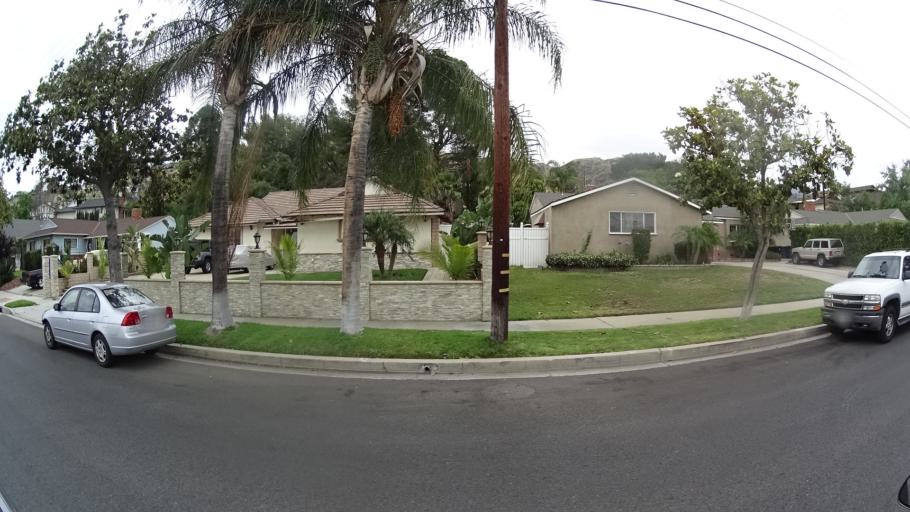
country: US
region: California
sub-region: Los Angeles County
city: Burbank
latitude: 34.2037
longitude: -118.3232
